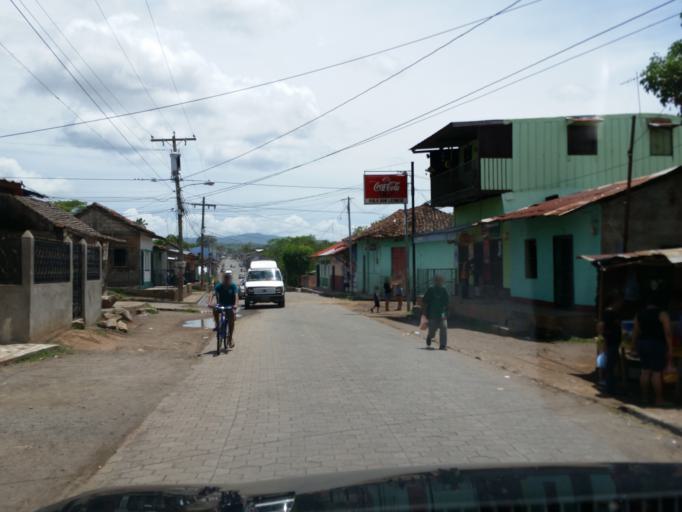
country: NI
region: Granada
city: Granada
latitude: 11.9241
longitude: -85.9530
